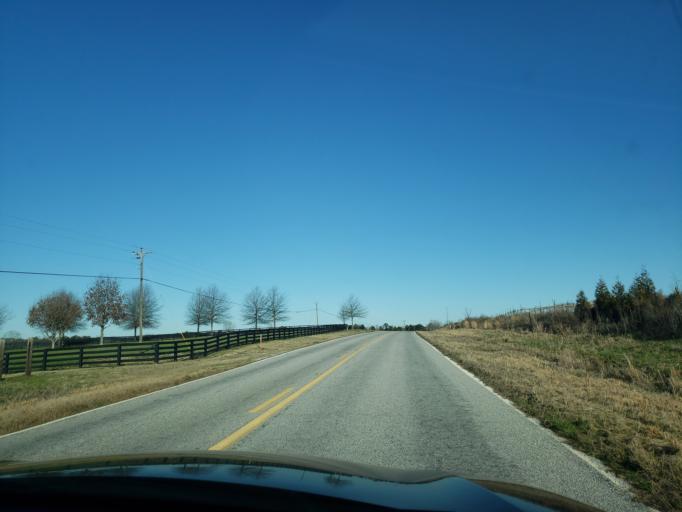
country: US
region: Alabama
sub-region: Elmore County
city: Tallassee
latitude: 32.5872
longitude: -85.7954
